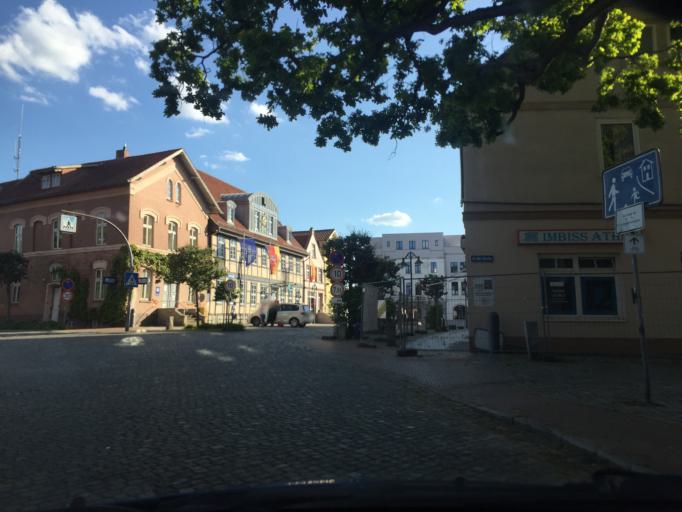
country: DE
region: Lower Saxony
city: Dannenberg
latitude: 53.0994
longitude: 11.0967
